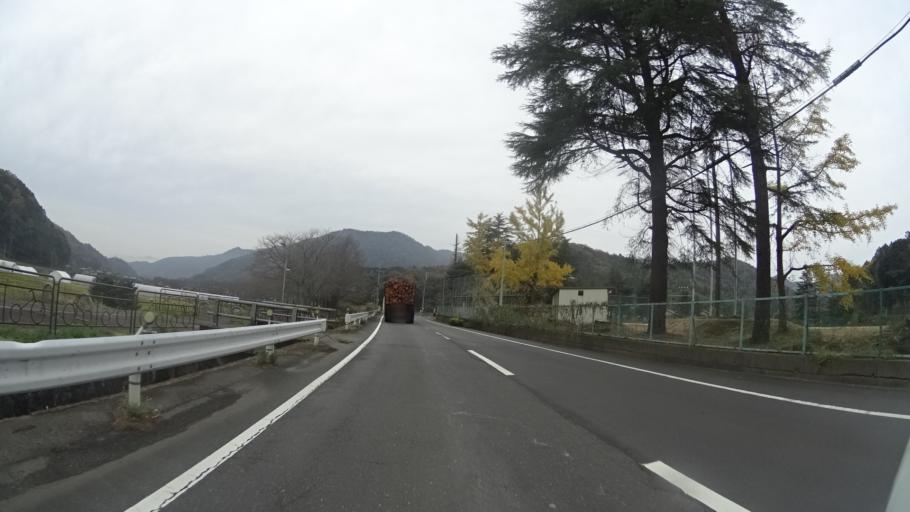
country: JP
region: Kyoto
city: Maizuru
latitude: 35.4965
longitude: 135.4377
